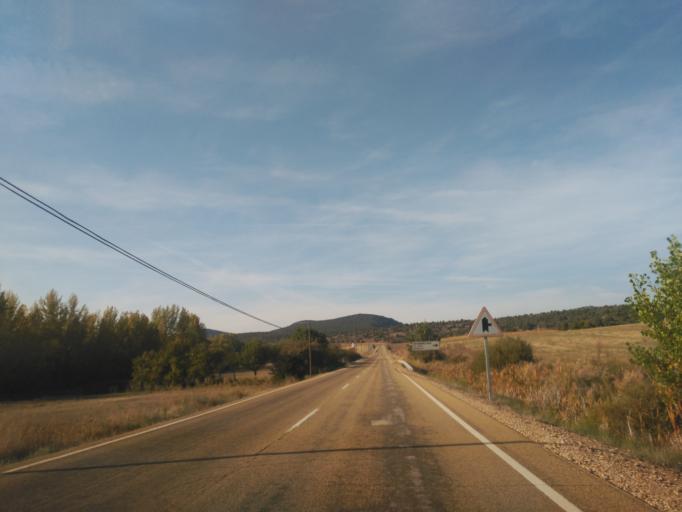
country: ES
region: Castille and Leon
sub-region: Provincia de Soria
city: Ucero
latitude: 41.7051
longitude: -3.0454
